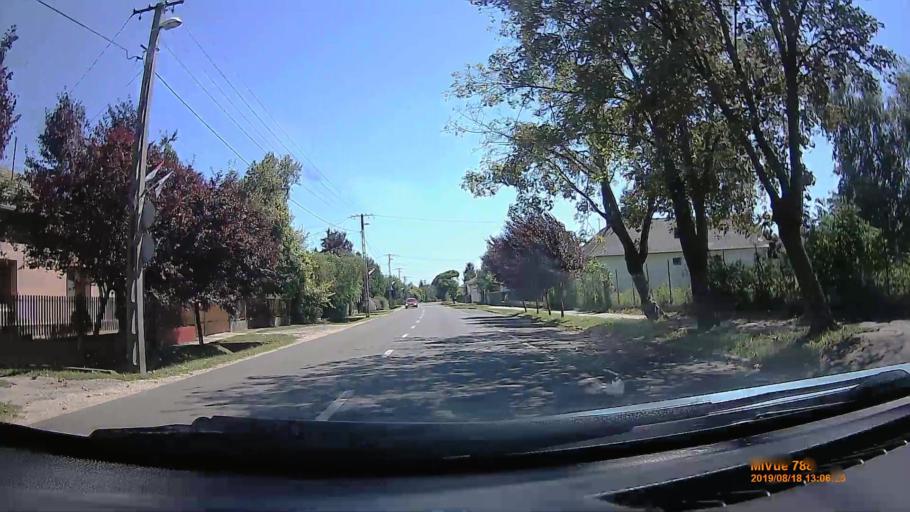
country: HU
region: Fejer
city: Kaloz
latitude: 46.9570
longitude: 18.4901
